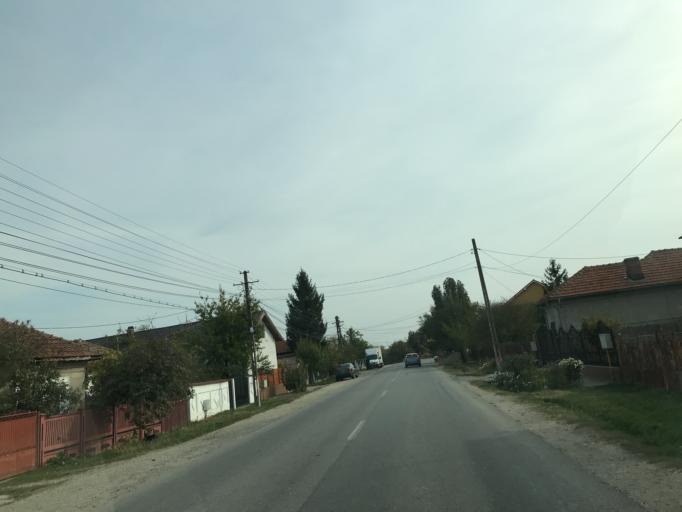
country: RO
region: Olt
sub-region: Comuna Slatioara
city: Slatioara
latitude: 44.4080
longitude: 24.3266
